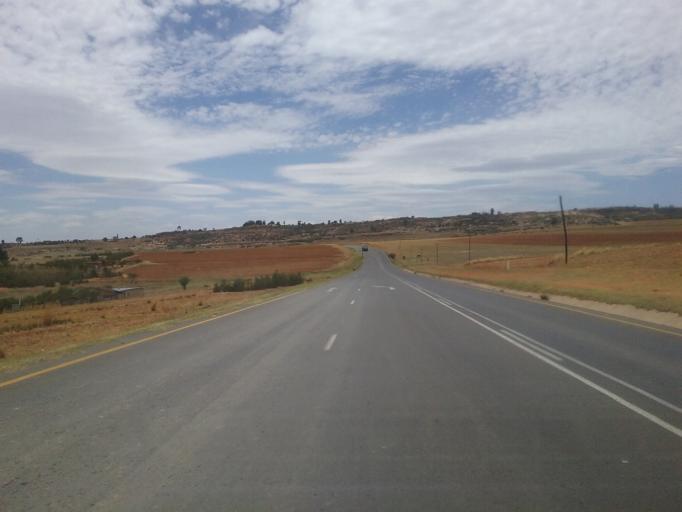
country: LS
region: Maseru
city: Maseru
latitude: -29.5086
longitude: 27.5243
